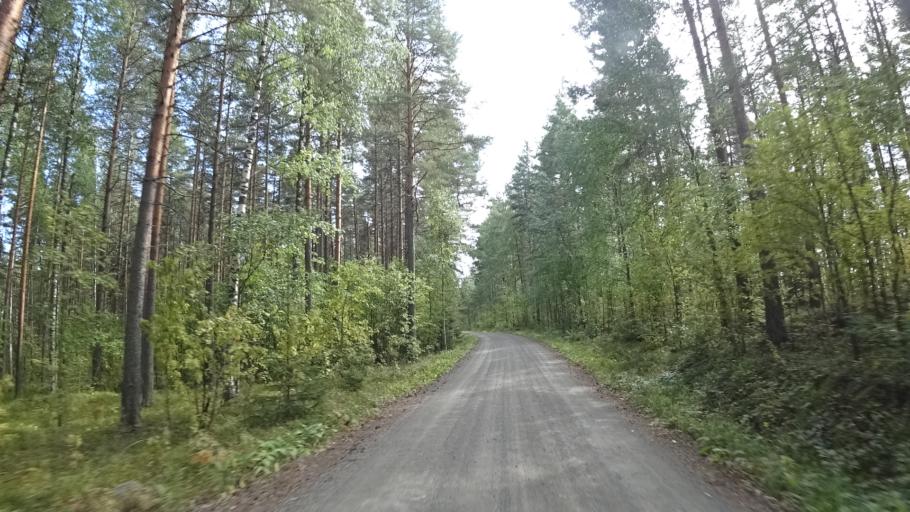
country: FI
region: North Karelia
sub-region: Keski-Karjala
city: Raeaekkylae
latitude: 62.3938
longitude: 29.7703
